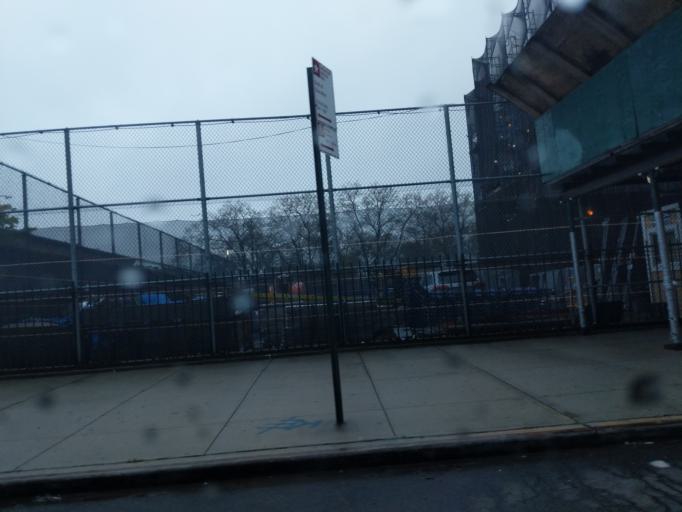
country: US
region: New York
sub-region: Kings County
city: East New York
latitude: 40.6969
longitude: -73.9106
